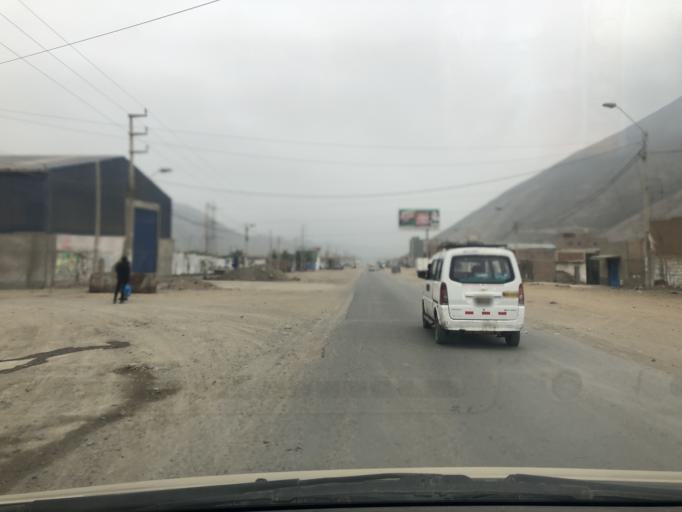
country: PE
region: Lima
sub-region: Lima
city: Cieneguilla
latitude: -12.1543
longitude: -76.8693
